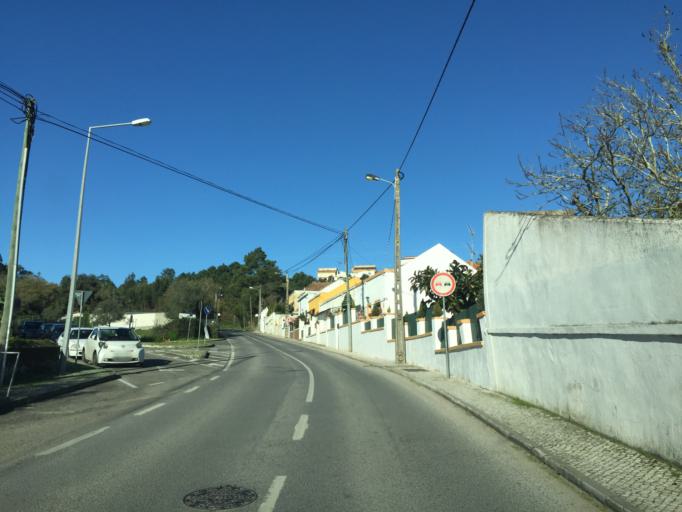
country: PT
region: Lisbon
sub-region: Odivelas
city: Canecas
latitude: 38.8183
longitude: -9.2292
